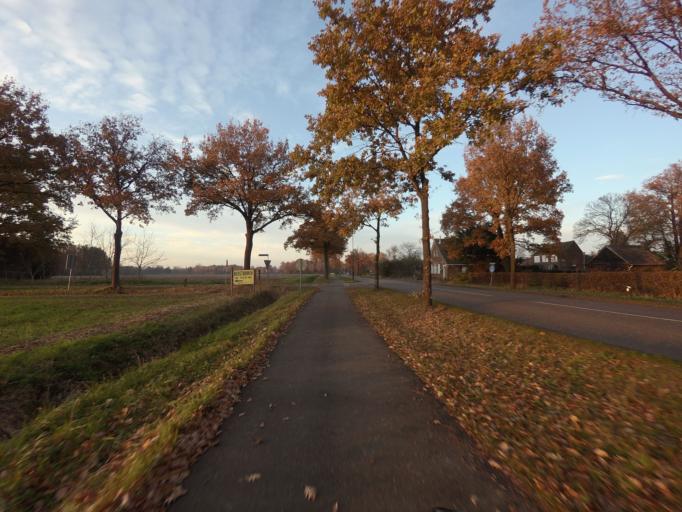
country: NL
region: North Brabant
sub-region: Gemeente Breda
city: Breda
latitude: 51.5284
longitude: 4.7921
